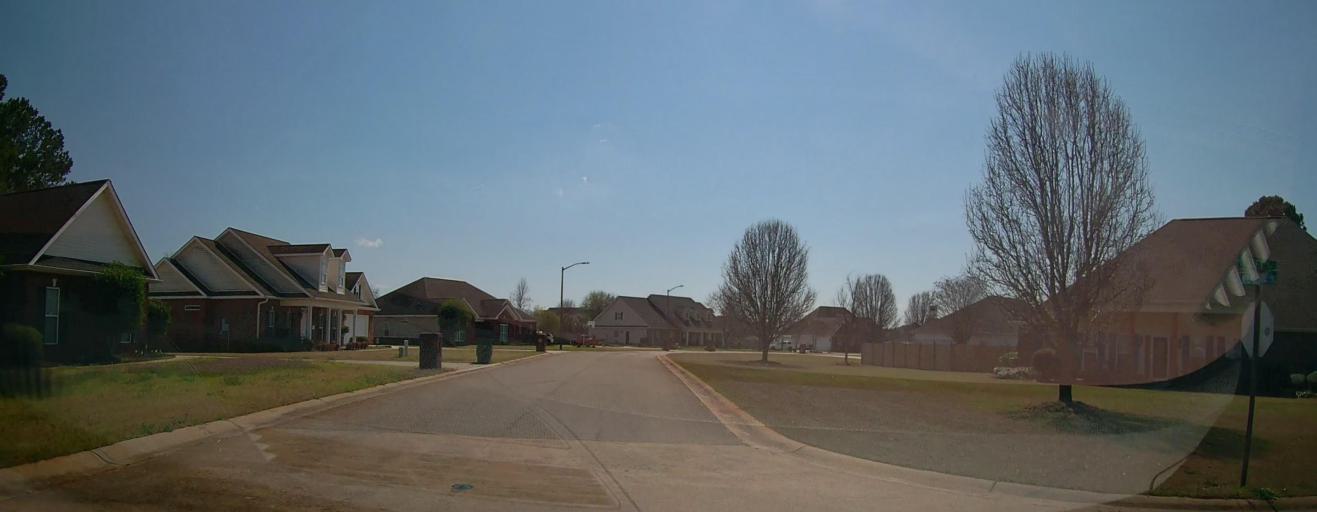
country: US
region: Georgia
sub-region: Houston County
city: Centerville
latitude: 32.5844
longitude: -83.7126
